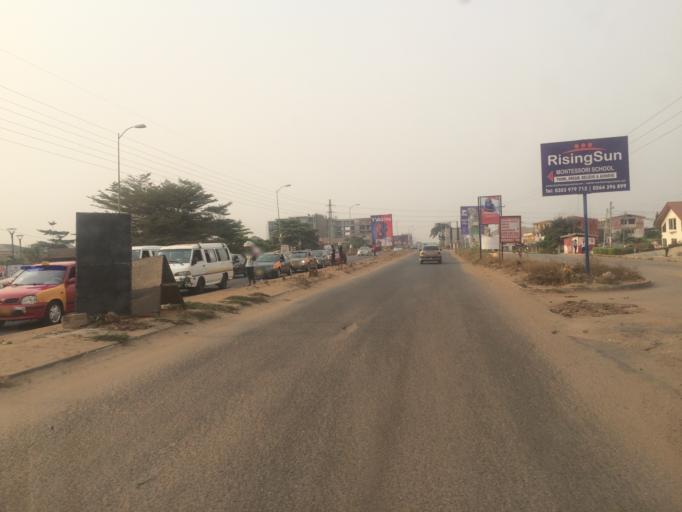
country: GH
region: Greater Accra
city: Nungua
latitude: 5.6211
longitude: -0.0706
